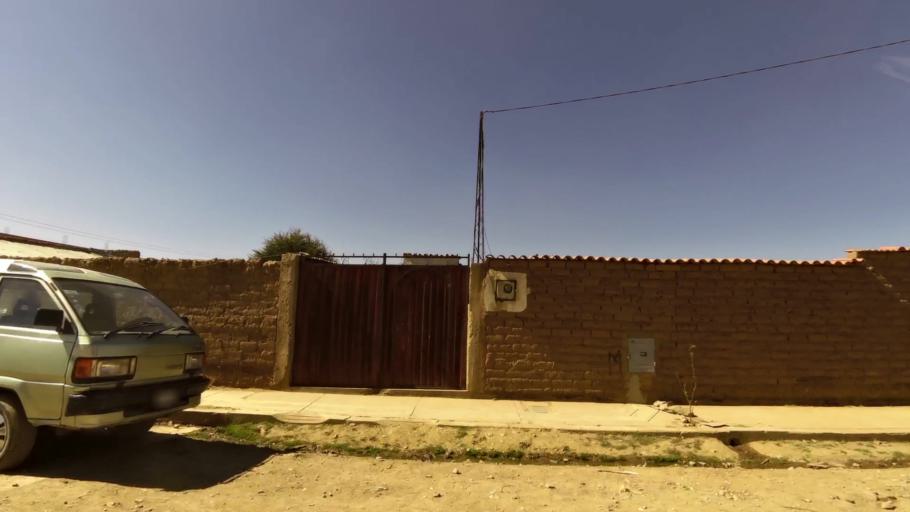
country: BO
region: La Paz
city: La Paz
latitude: -16.5851
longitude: -68.2088
